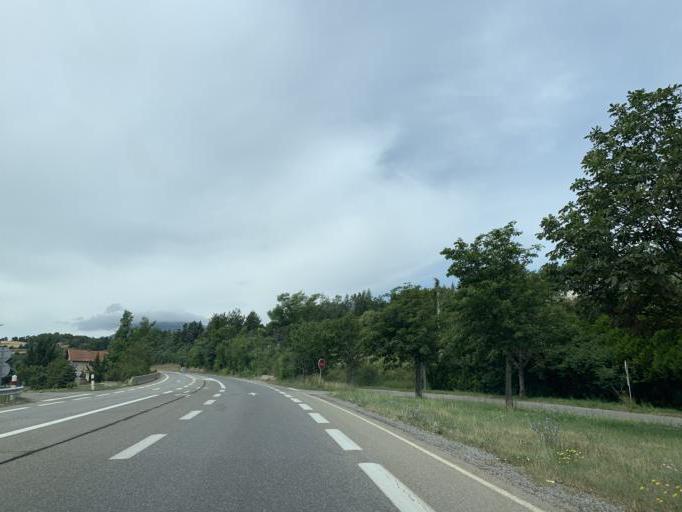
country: FR
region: Provence-Alpes-Cote d'Azur
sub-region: Departement des Hautes-Alpes
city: Gap
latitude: 44.5563
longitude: 6.0444
